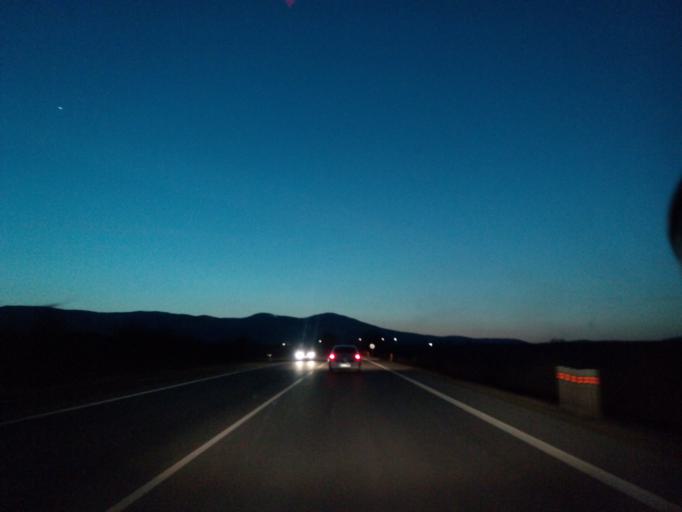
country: SK
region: Kosicky
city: Secovce
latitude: 48.7053
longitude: 21.6326
